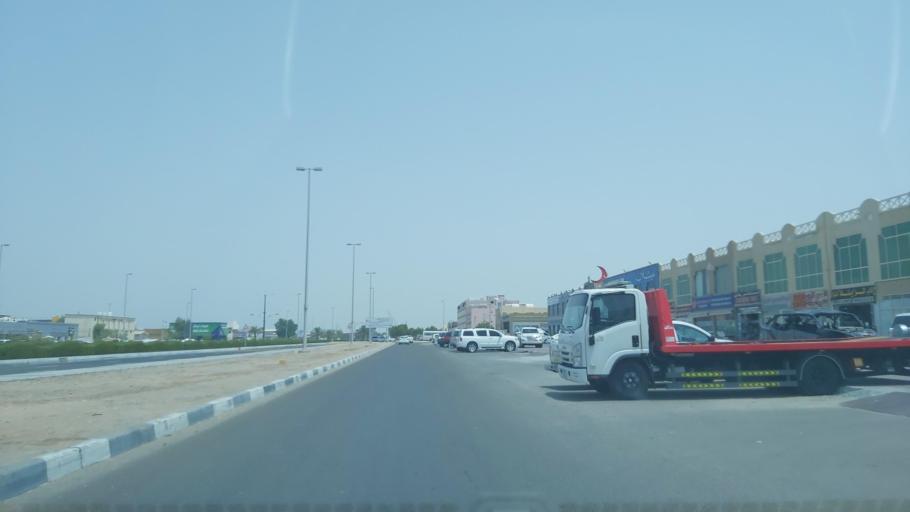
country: AE
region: Abu Dhabi
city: Abu Dhabi
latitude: 24.3756
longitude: 54.5163
